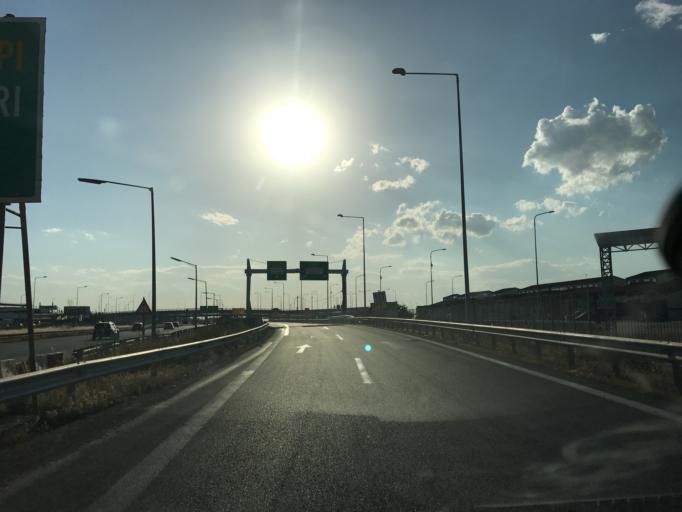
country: GR
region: Central Macedonia
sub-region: Nomos Thessalonikis
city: Menemeni
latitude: 40.6557
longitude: 22.8871
